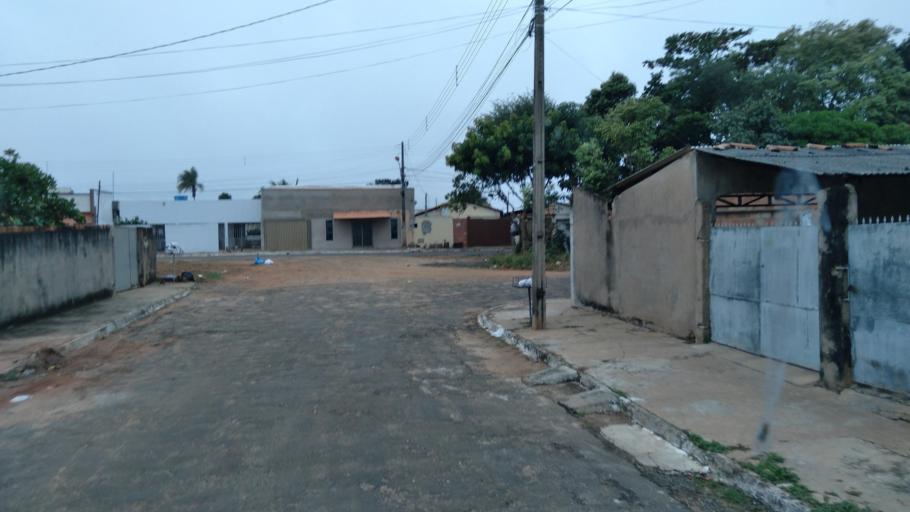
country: BR
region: Goias
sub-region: Mineiros
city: Mineiros
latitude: -17.5748
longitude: -52.5404
